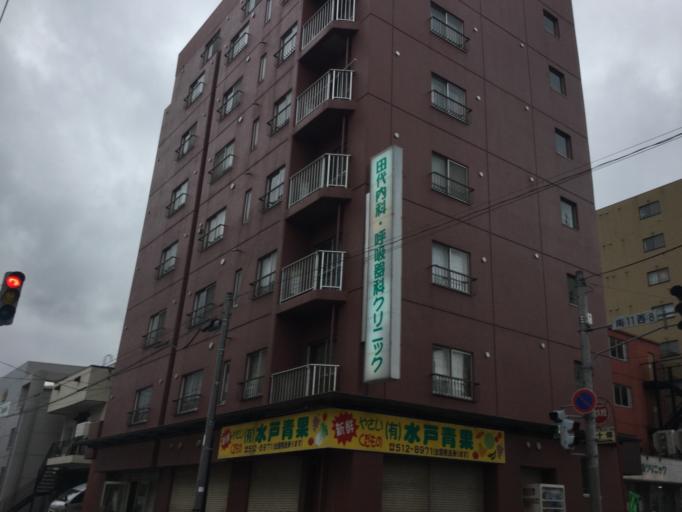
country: JP
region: Hokkaido
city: Sapporo
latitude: 43.0456
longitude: 141.3485
